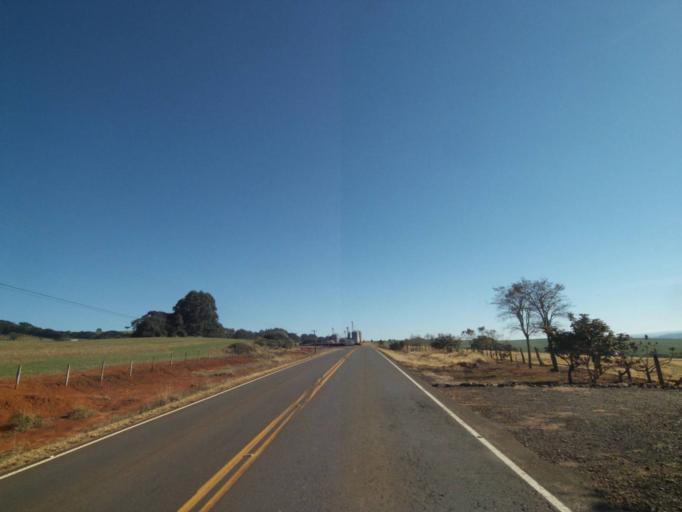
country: BR
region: Parana
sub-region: Tibagi
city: Tibagi
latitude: -24.5074
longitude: -50.4362
